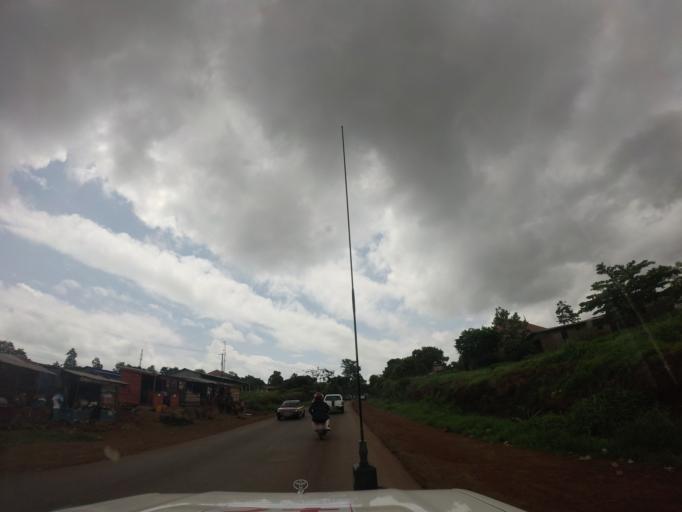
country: SL
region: Western Area
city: Hastings
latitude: 8.3844
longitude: -13.1120
